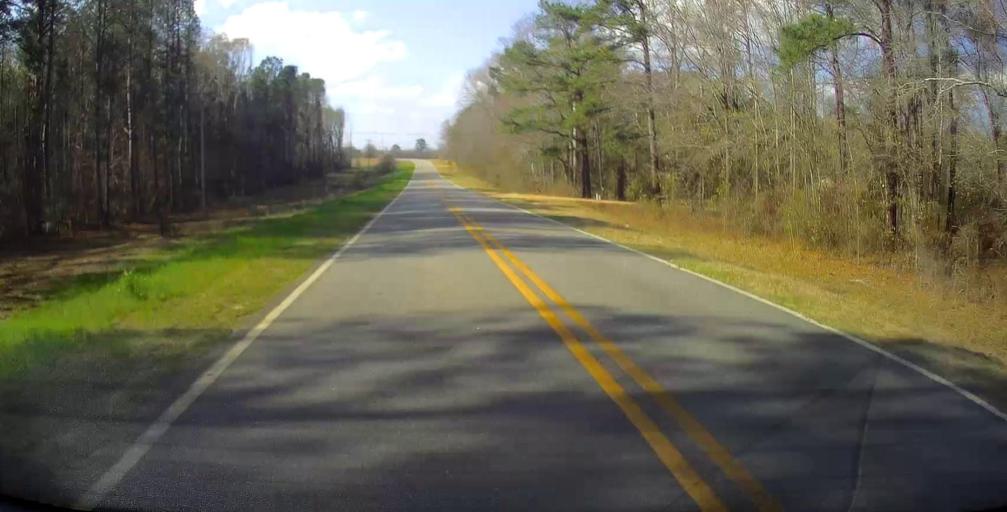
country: US
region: Georgia
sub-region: Wilkinson County
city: Irwinton
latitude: 32.6235
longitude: -83.0910
